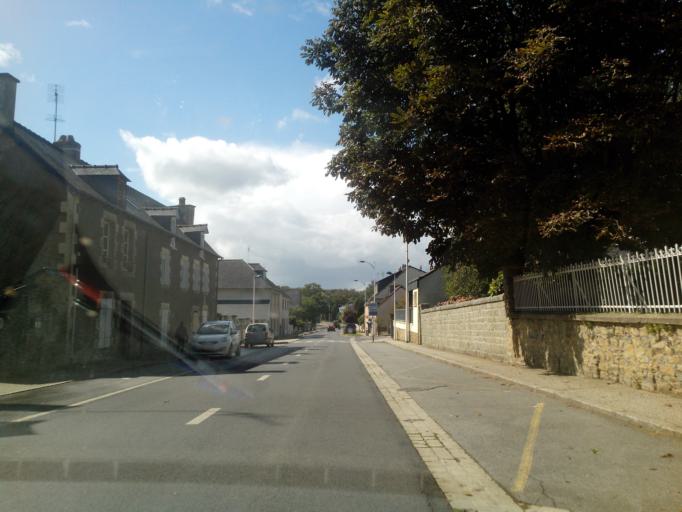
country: FR
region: Brittany
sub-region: Departement des Cotes-d'Armor
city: Merdrignac
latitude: 48.1916
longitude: -2.4162
